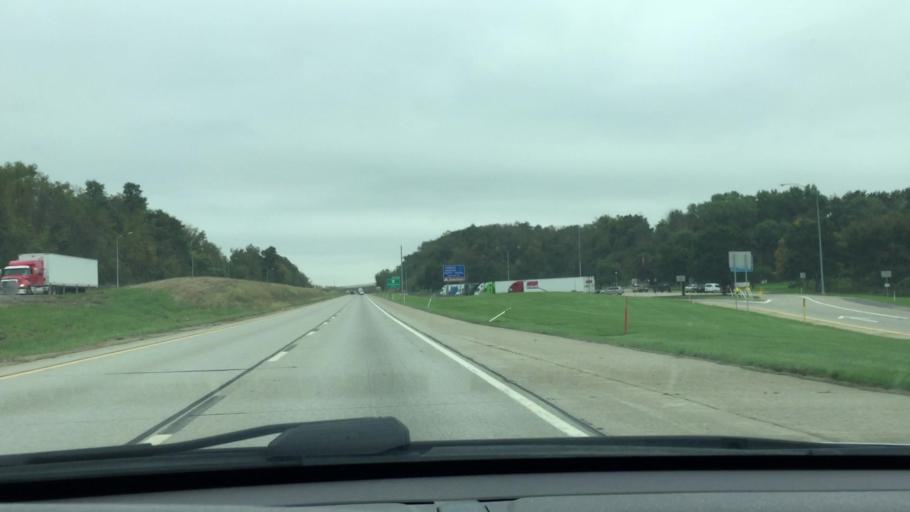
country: US
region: Pennsylvania
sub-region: Allegheny County
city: Bridgeville
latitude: 40.3300
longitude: -80.1392
